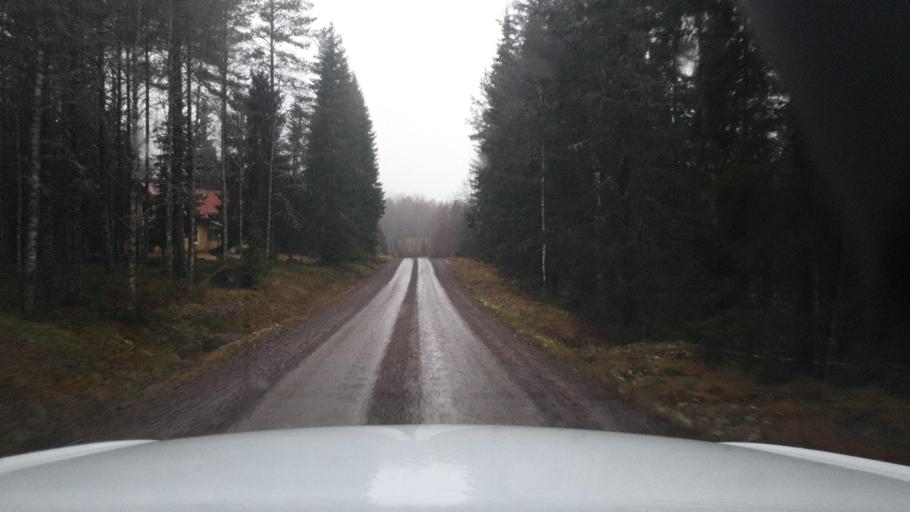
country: SE
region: Vaermland
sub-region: Arvika Kommun
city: Arvika
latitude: 59.9958
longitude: 12.6612
